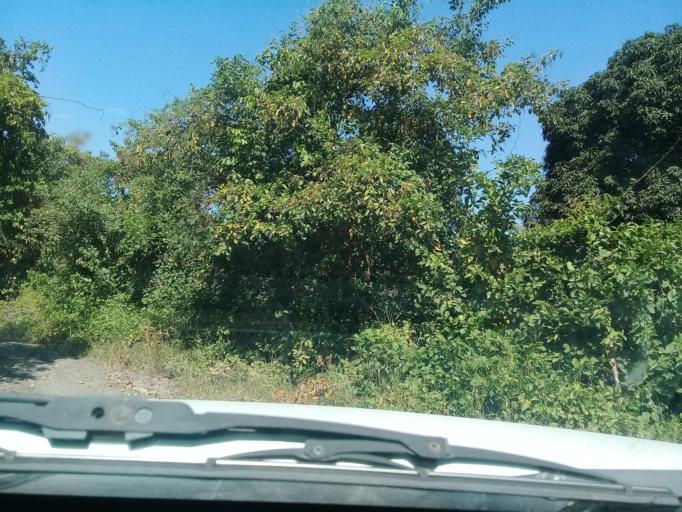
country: MX
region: Veracruz
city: Actopan
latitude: 19.4396
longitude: -96.5628
